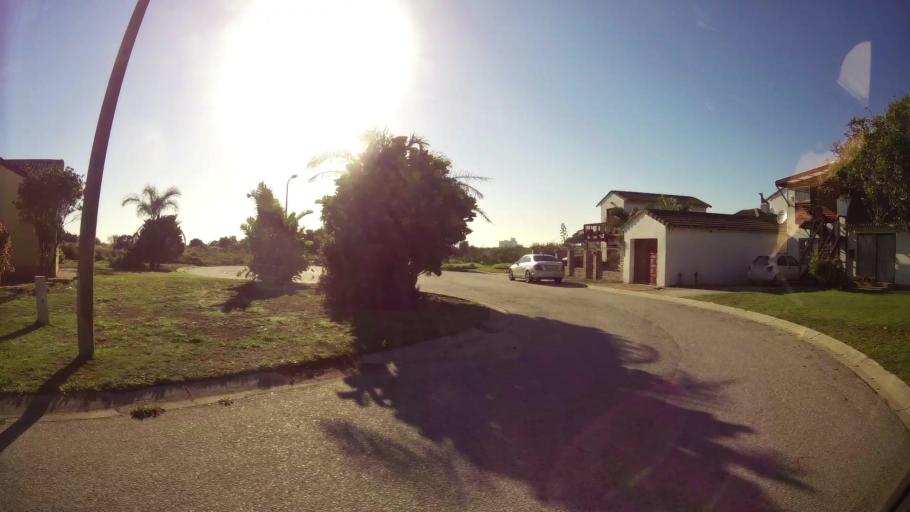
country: ZA
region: Eastern Cape
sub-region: Nelson Mandela Bay Metropolitan Municipality
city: Port Elizabeth
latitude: -33.9781
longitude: 25.6319
